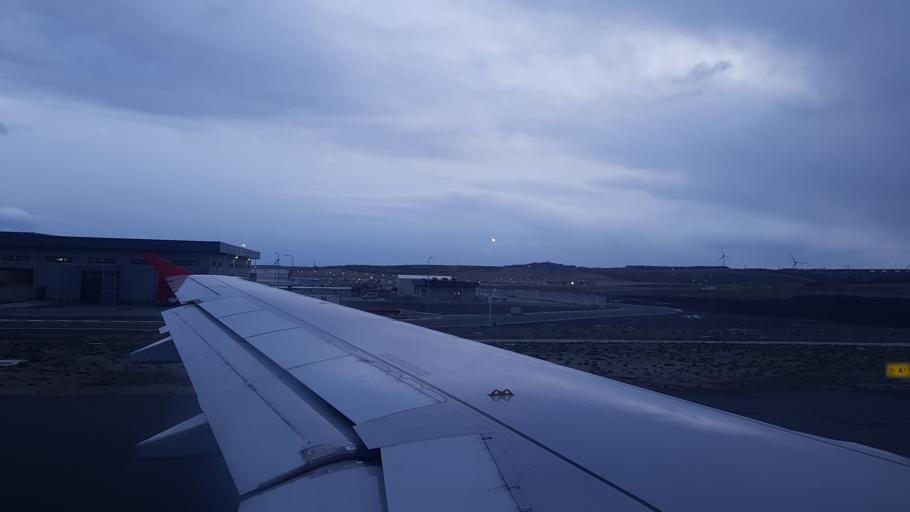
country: TR
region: Istanbul
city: Durusu
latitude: 41.2650
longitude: 28.7126
